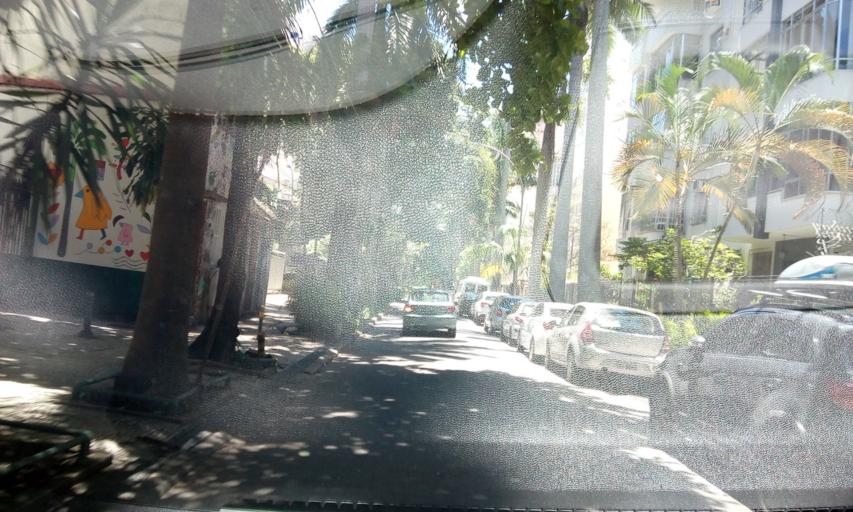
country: BR
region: Rio de Janeiro
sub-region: Rio De Janeiro
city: Rio de Janeiro
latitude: -22.9359
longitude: -43.1803
